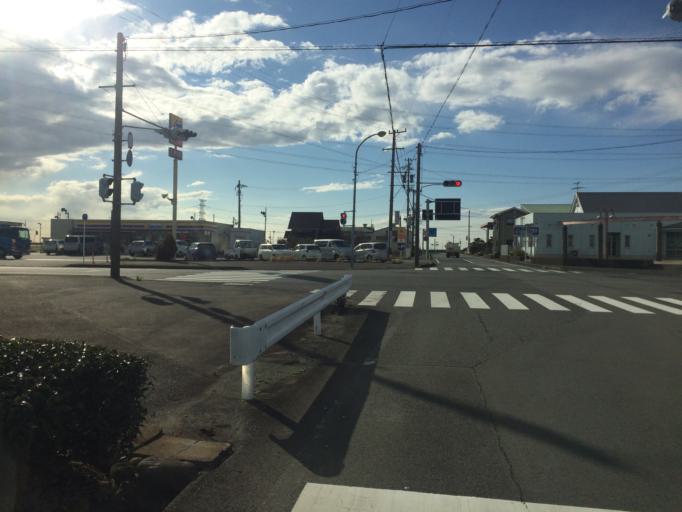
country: JP
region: Shizuoka
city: Kanaya
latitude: 34.7653
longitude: 138.1405
